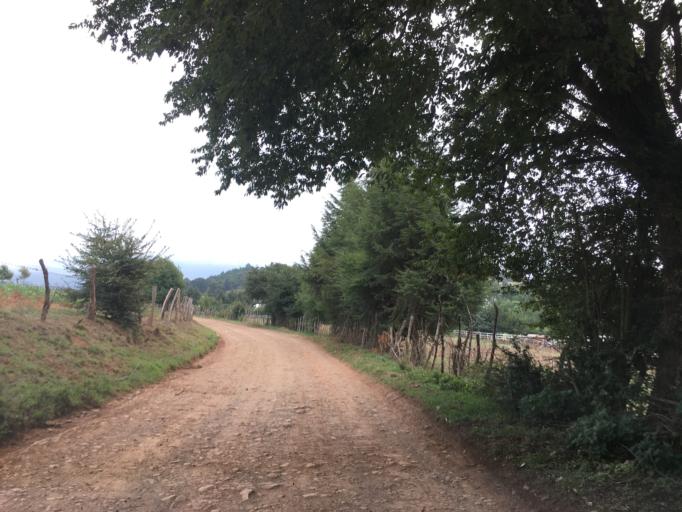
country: MX
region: Michoacan
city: Acuitzio del Canje
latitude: 19.4904
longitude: -101.2383
